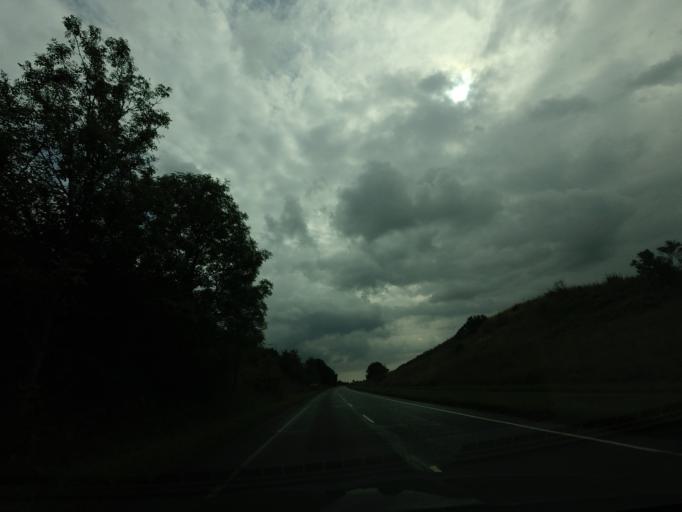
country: GB
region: Scotland
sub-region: Dumfries and Galloway
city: Lockerbie
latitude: 55.1313
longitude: -3.3635
